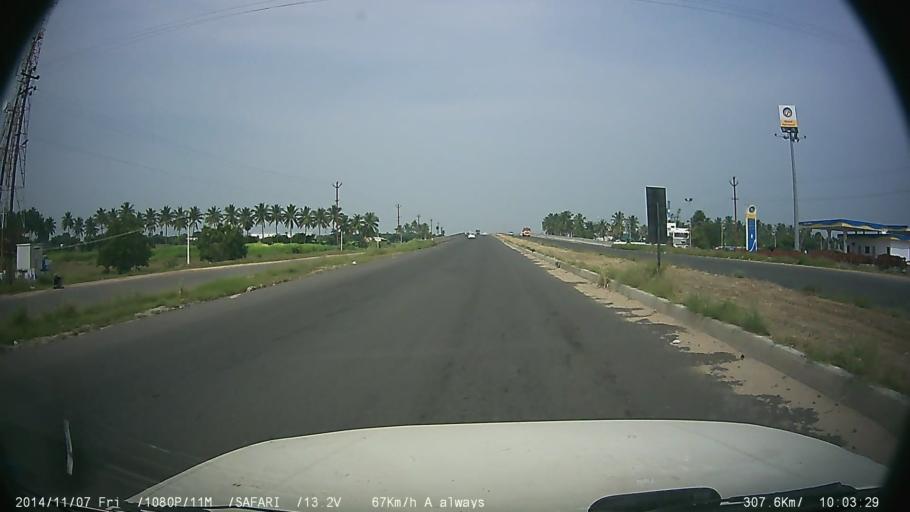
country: IN
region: Tamil Nadu
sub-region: Tiruppur
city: Uttukkuli
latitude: 11.2041
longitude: 77.3937
